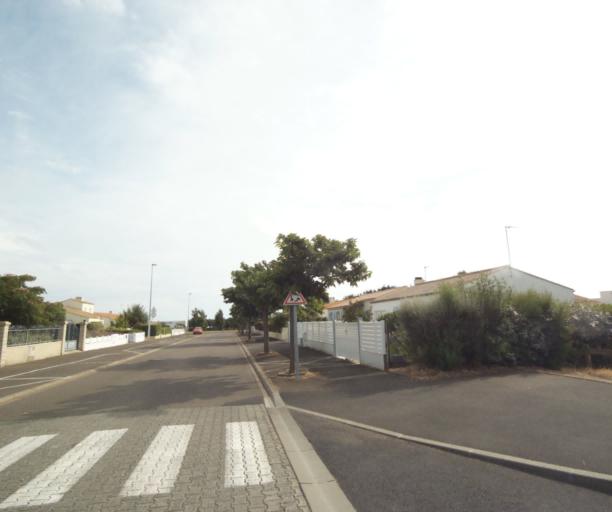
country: FR
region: Pays de la Loire
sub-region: Departement de la Vendee
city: Chateau-d'Olonne
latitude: 46.4893
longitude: -1.7443
